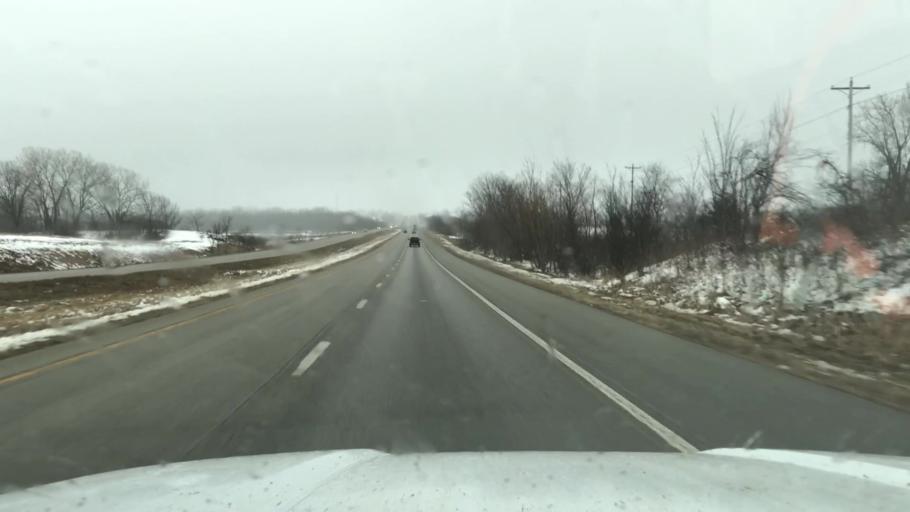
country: US
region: Missouri
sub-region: Clinton County
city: Gower
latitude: 39.7474
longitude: -94.6729
